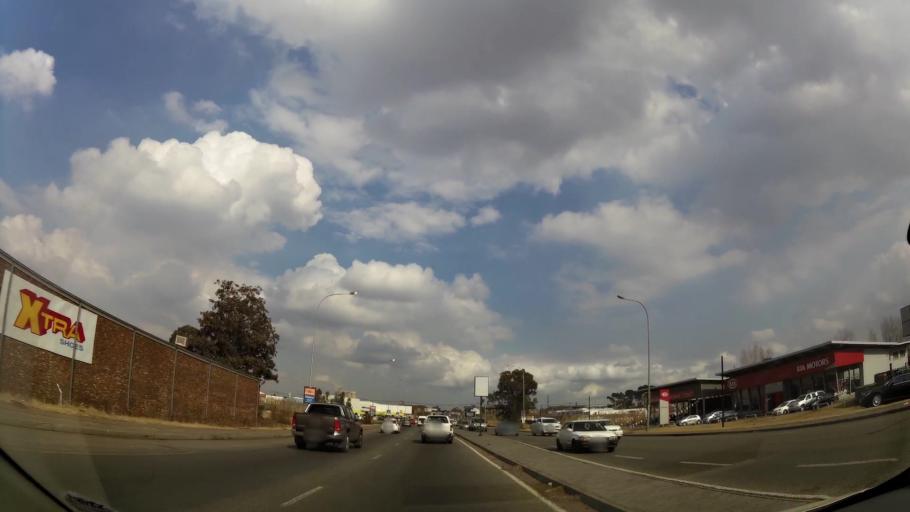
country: ZA
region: Gauteng
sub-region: Sedibeng District Municipality
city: Vereeniging
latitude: -26.6630
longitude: 27.9343
